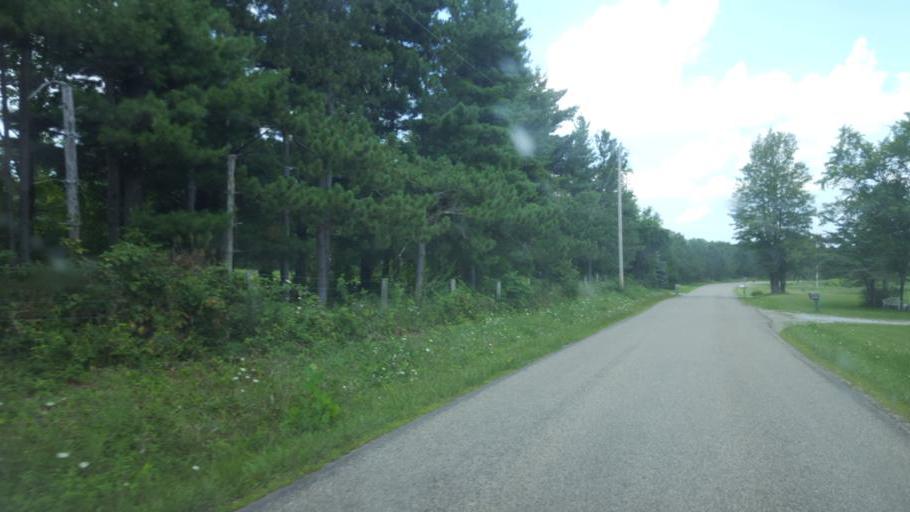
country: US
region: Ohio
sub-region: Knox County
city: Fredericktown
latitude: 40.3863
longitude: -82.6046
